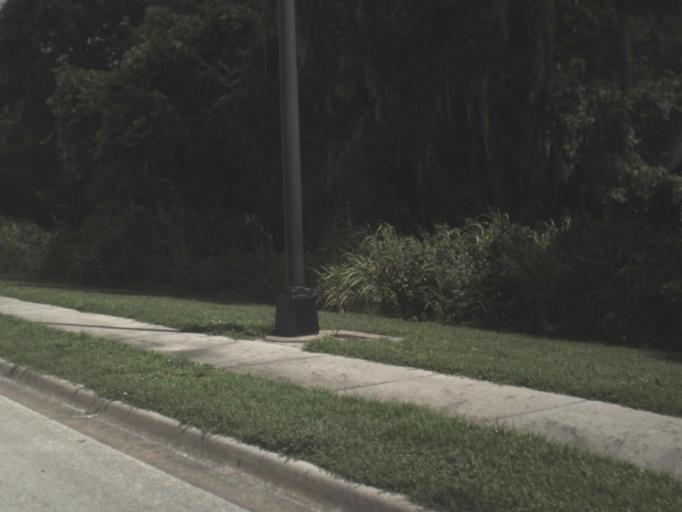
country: US
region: Florida
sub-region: Hardee County
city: Wauchula
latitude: 27.5302
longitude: -81.8063
